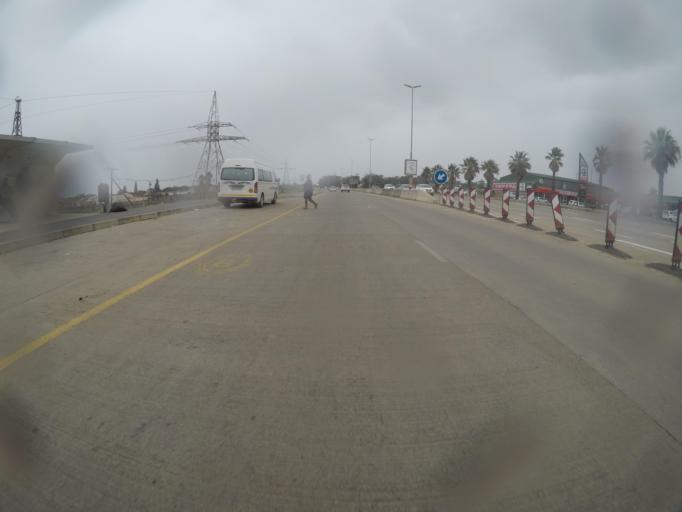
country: ZA
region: Eastern Cape
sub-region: Buffalo City Metropolitan Municipality
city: East London
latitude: -32.9350
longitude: 27.9924
